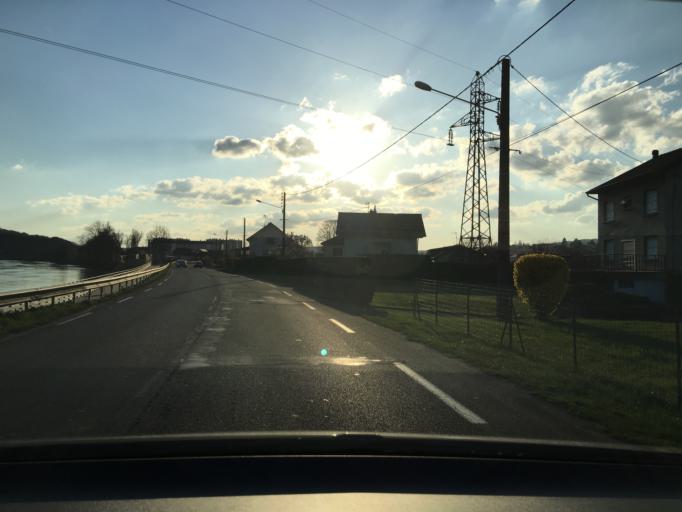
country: FR
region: Franche-Comte
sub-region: Departement du Doubs
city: Bavans
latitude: 47.4807
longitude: 6.7444
